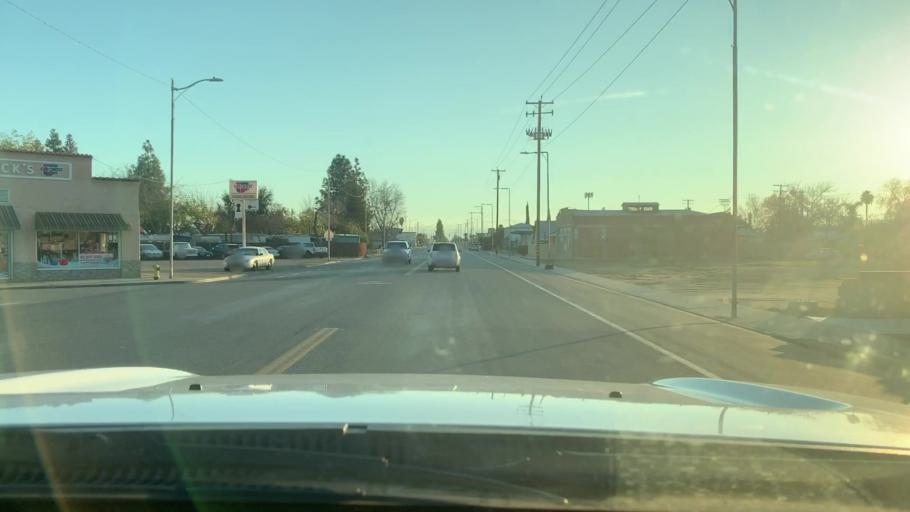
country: US
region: California
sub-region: Kern County
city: Shafter
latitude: 35.4998
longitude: -119.2756
